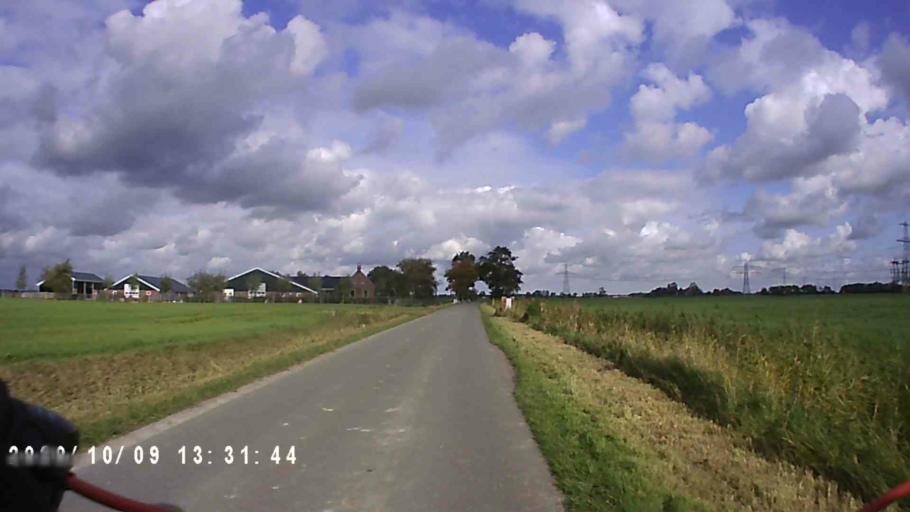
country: NL
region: Groningen
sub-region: Gemeente Zuidhorn
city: Aduard
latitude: 53.2819
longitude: 6.4723
